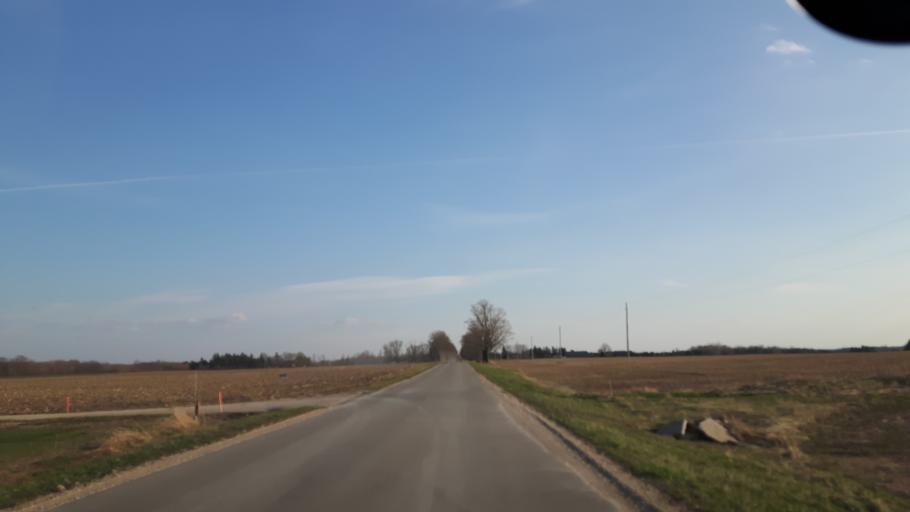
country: CA
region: Ontario
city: Goderich
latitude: 43.6320
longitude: -81.6643
